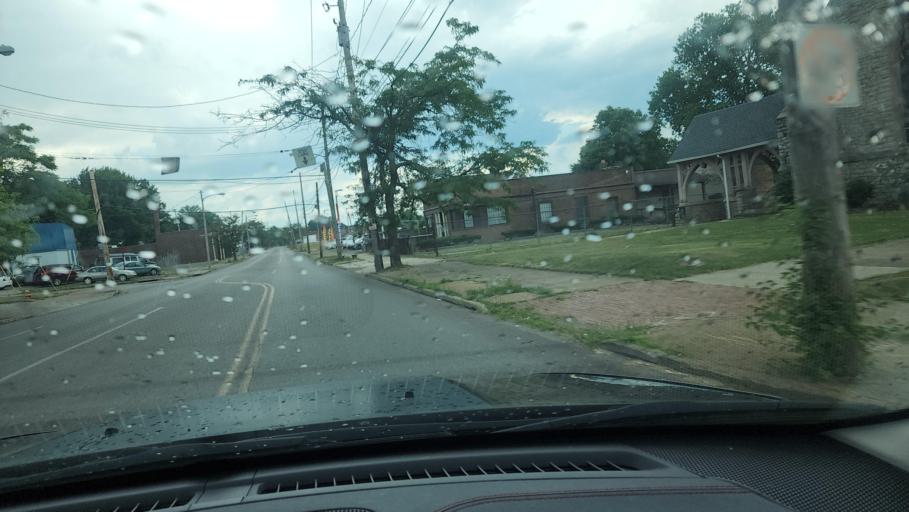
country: US
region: Ohio
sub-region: Mahoning County
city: Youngstown
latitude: 41.1106
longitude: -80.6408
